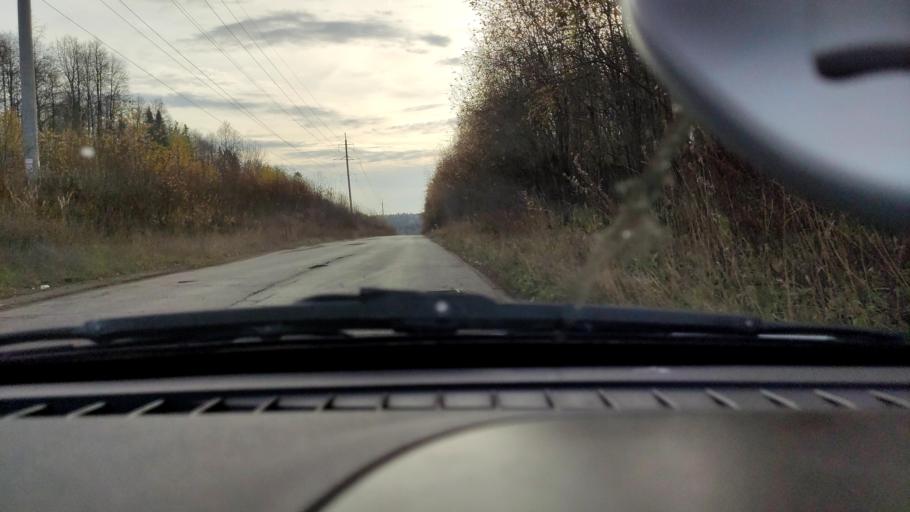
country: RU
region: Perm
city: Perm
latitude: 58.0917
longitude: 56.4105
